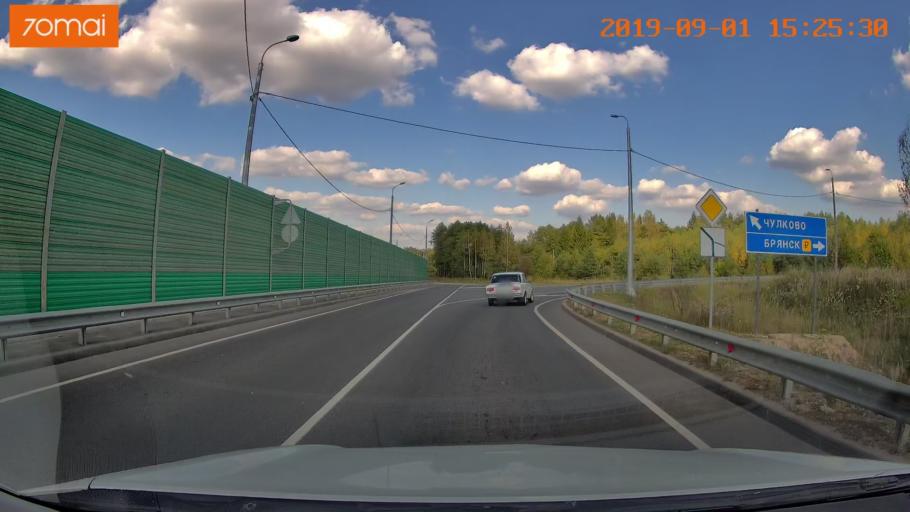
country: RU
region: Kaluga
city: Maloyaroslavets
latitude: 54.9603
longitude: 36.4581
